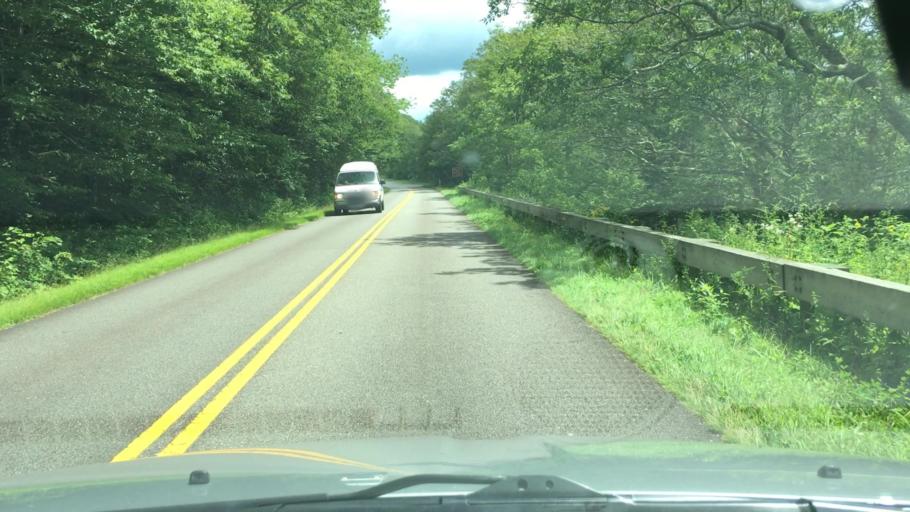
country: US
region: North Carolina
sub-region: Buncombe County
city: Black Mountain
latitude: 35.7200
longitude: -82.2813
